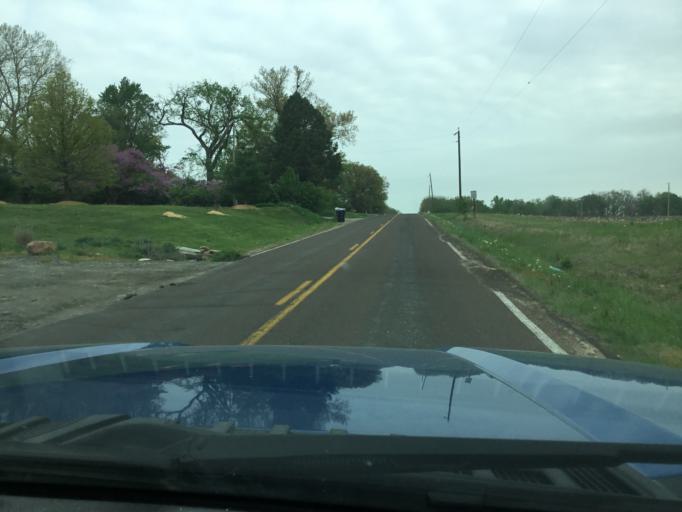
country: US
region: Kansas
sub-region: Shawnee County
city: Topeka
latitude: 39.1038
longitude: -95.7247
